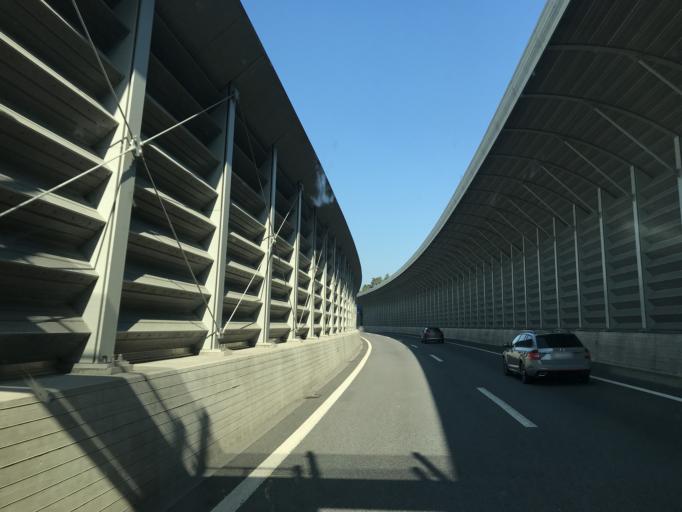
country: IT
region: Lombardy
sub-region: Provincia di Como
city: Campione
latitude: 45.9486
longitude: 8.9670
